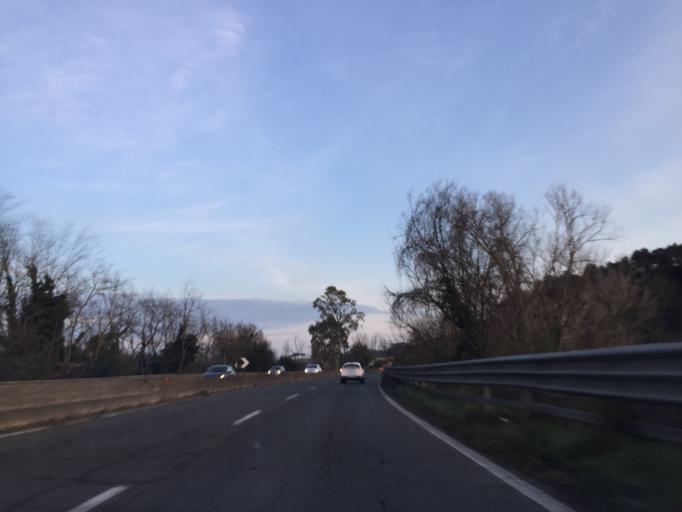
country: IT
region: Latium
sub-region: Citta metropolitana di Roma Capitale
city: Monte Caminetto
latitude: 41.9944
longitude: 12.4661
